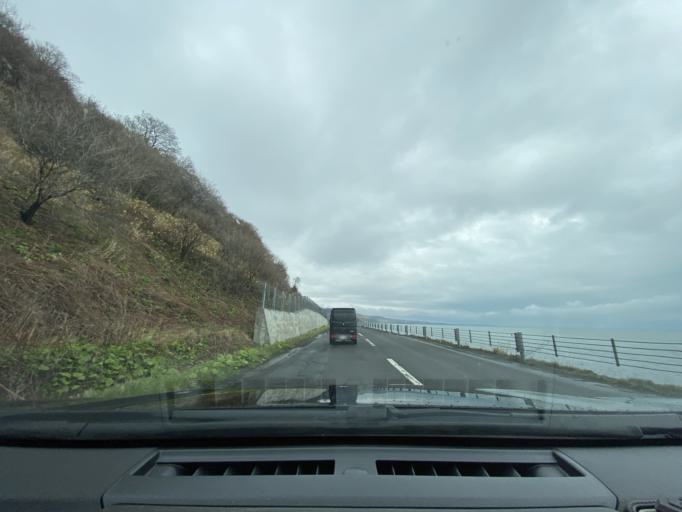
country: JP
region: Hokkaido
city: Ishikari
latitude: 43.4298
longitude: 141.4212
